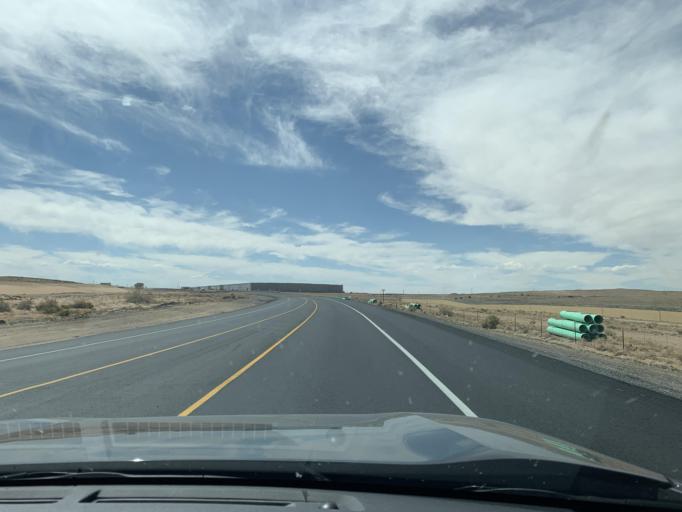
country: US
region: New Mexico
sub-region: Valencia County
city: Los Lunas
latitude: 34.8232
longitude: -106.8020
